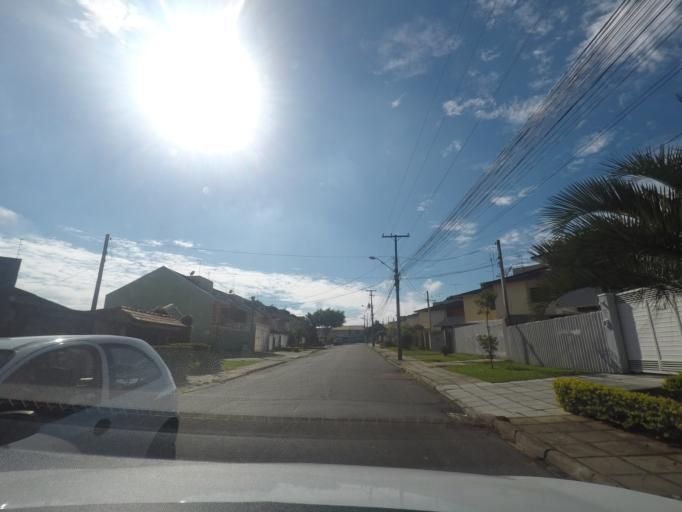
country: BR
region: Parana
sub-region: Sao Jose Dos Pinhais
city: Sao Jose dos Pinhais
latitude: -25.5047
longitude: -49.2598
